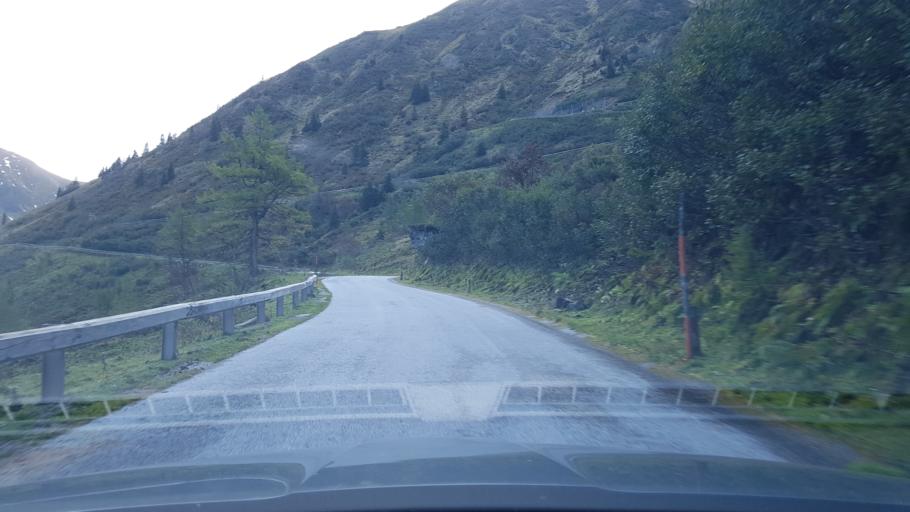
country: AT
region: Styria
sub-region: Politischer Bezirk Liezen
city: Sankt Nikolai im Solktal
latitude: 47.2770
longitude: 14.0790
